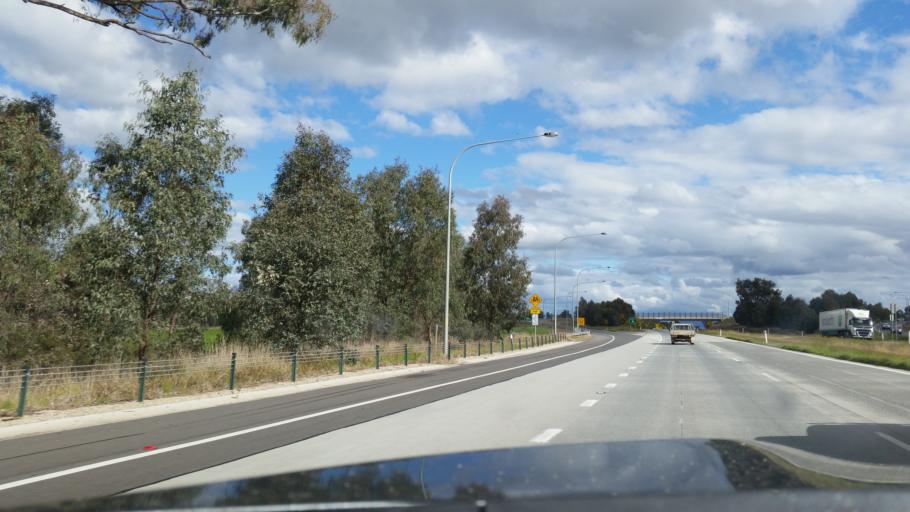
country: AU
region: New South Wales
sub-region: Albury Municipality
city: Lavington
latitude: -35.9976
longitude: 146.9929
